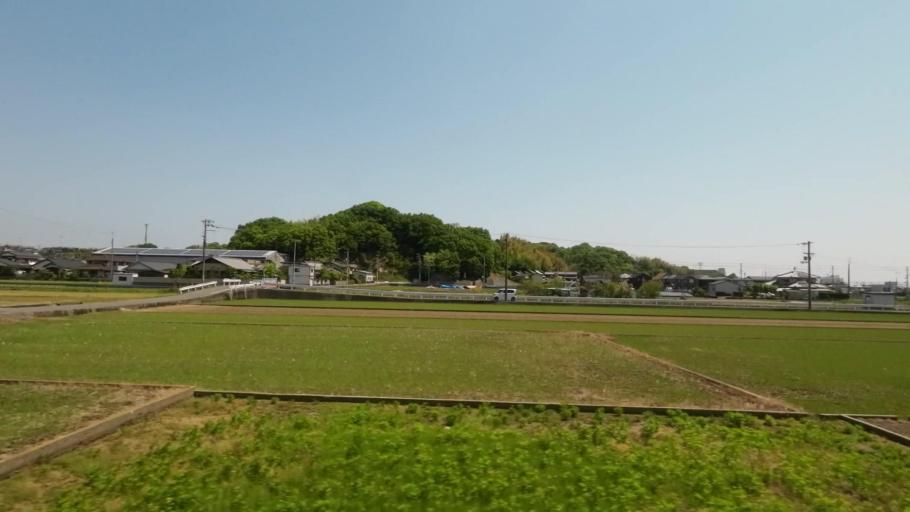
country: JP
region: Ehime
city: Saijo
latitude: 34.0214
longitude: 133.0265
